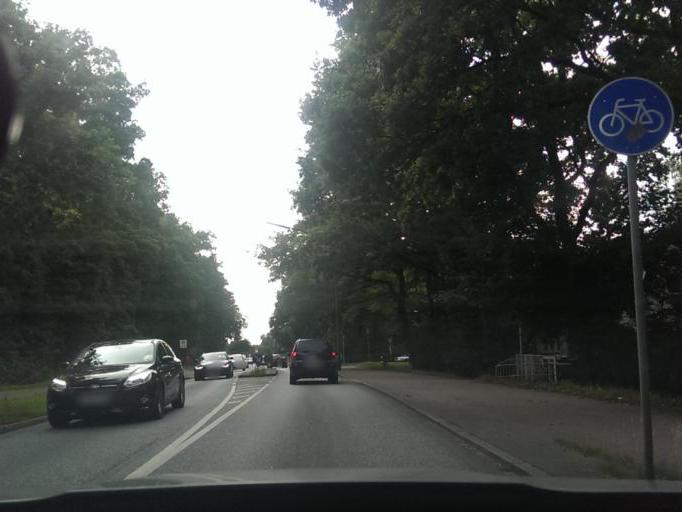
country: DE
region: Hamburg
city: Langenhorn
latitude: 53.6489
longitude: 9.9933
